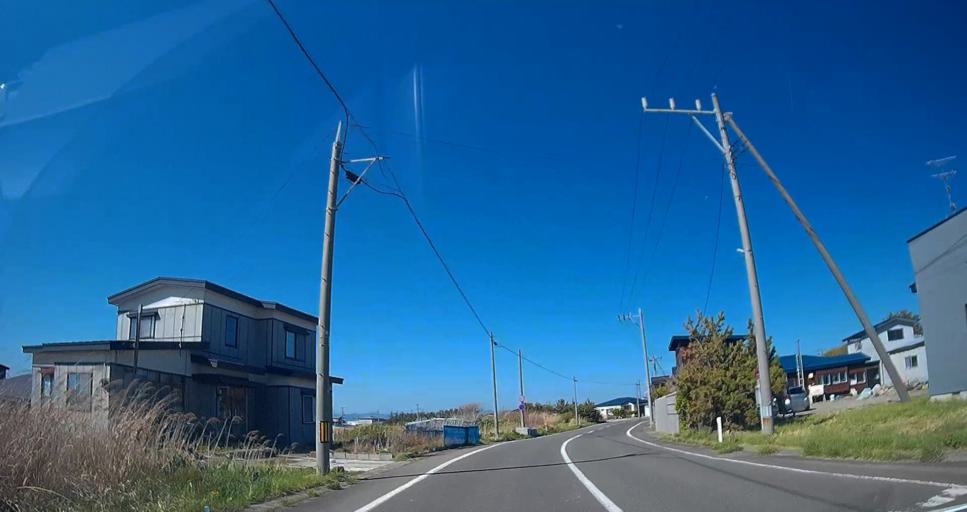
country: JP
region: Hokkaido
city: Hakodate
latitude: 41.5430
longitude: 140.9127
